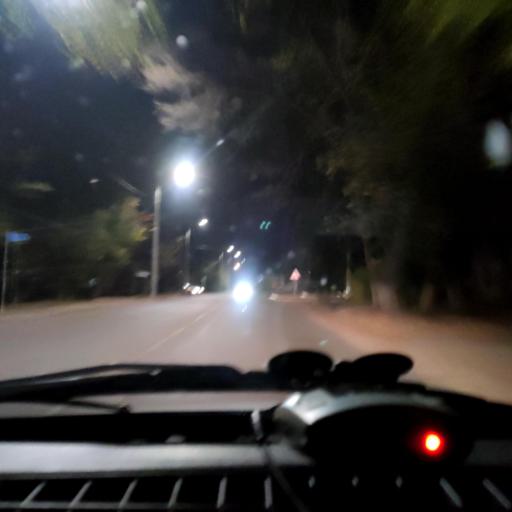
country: RU
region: Voronezj
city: Semiluki
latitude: 51.6788
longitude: 39.0300
